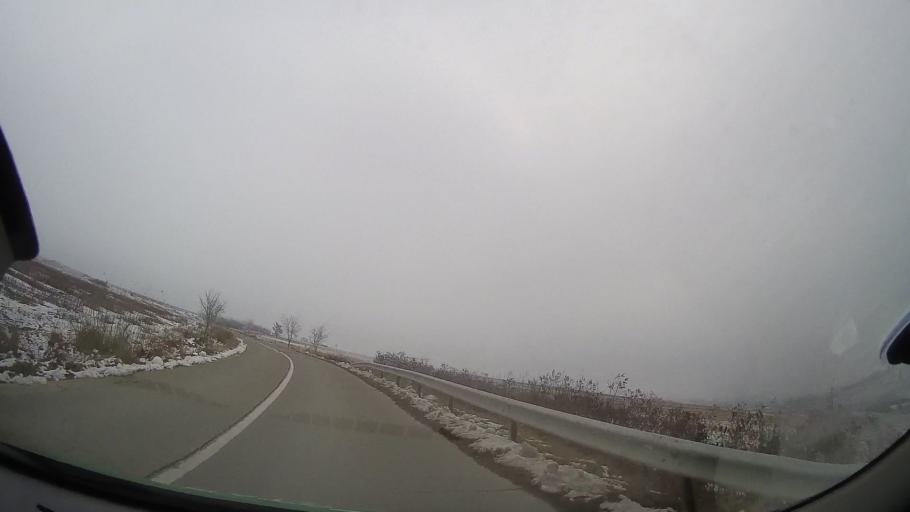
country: RO
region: Vaslui
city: Coroiesti
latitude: 46.2141
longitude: 27.4737
